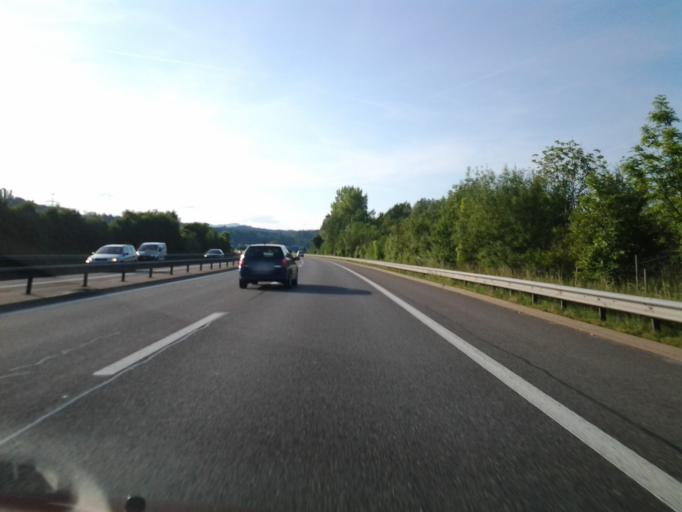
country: CH
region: Lucerne
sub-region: Willisau District
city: Reiden
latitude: 47.2322
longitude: 7.9695
